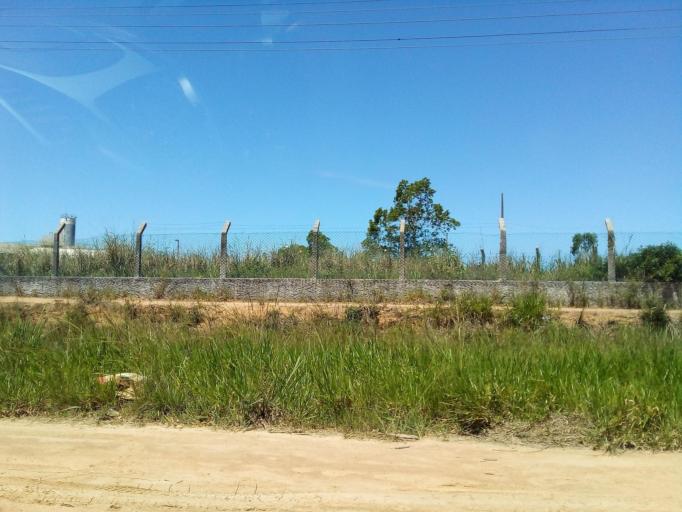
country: BR
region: Espirito Santo
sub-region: Aracruz
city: Aracruz
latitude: -19.8237
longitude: -40.0677
